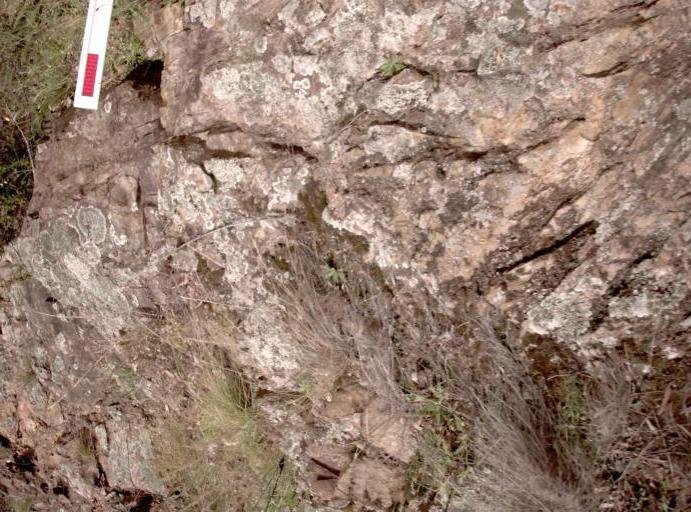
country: AU
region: Victoria
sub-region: Wellington
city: Heyfield
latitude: -37.7381
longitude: 146.6703
